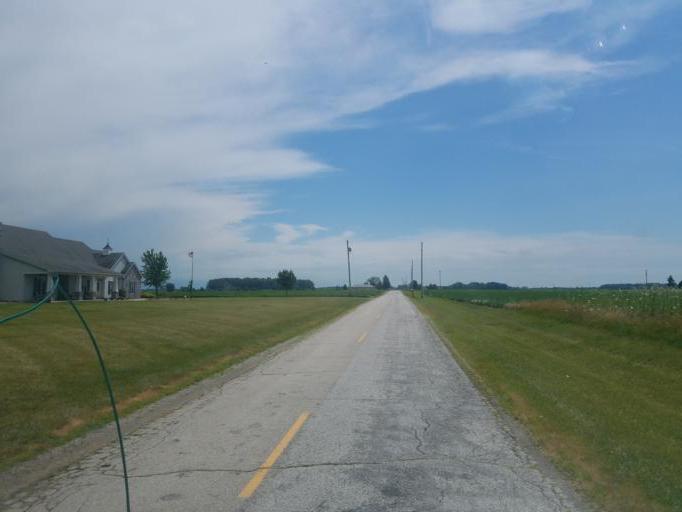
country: US
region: Ohio
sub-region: Paulding County
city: Antwerp
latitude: 41.2273
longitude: -84.7277
